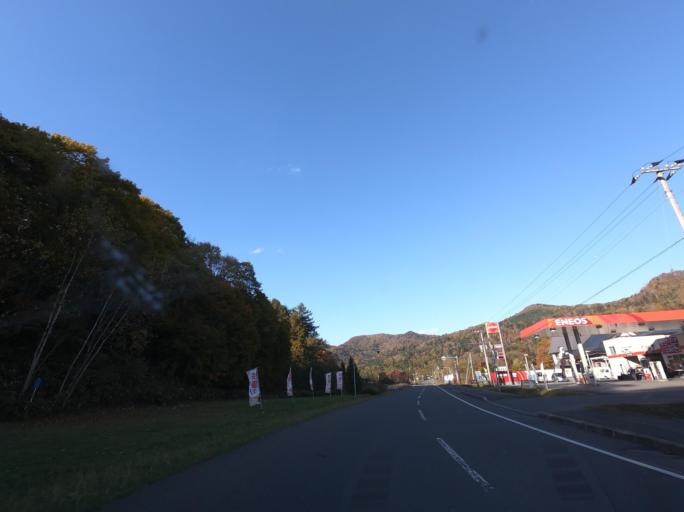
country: JP
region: Hokkaido
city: Iwamizawa
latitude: 43.0008
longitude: 142.0046
